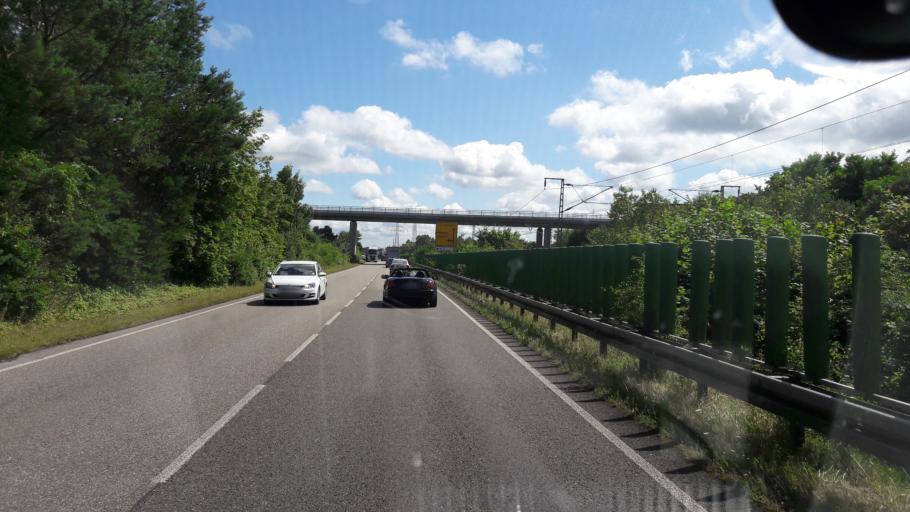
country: DE
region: Baden-Wuerttemberg
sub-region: Karlsruhe Region
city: Waghausel
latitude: 49.2308
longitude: 8.4961
